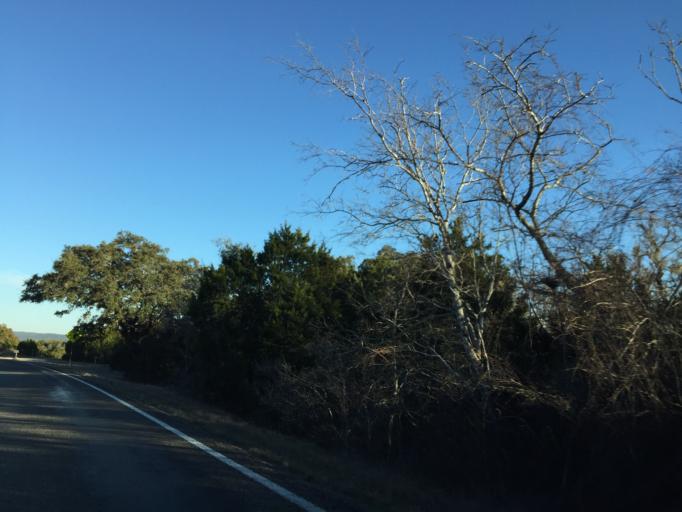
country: US
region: Texas
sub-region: Travis County
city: Lago Vista
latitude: 30.5193
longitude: -98.0737
